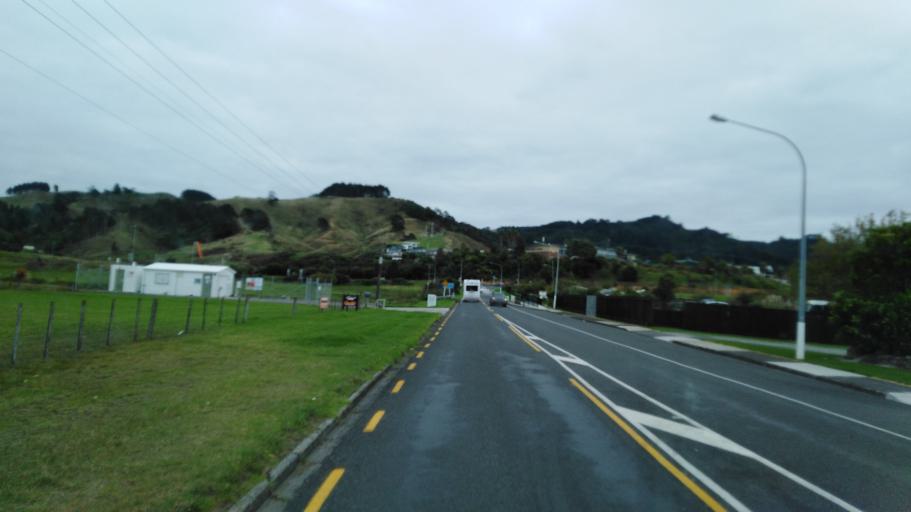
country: NZ
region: Bay of Plenty
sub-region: Western Bay of Plenty District
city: Waihi Beach
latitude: -37.4092
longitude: 175.9379
